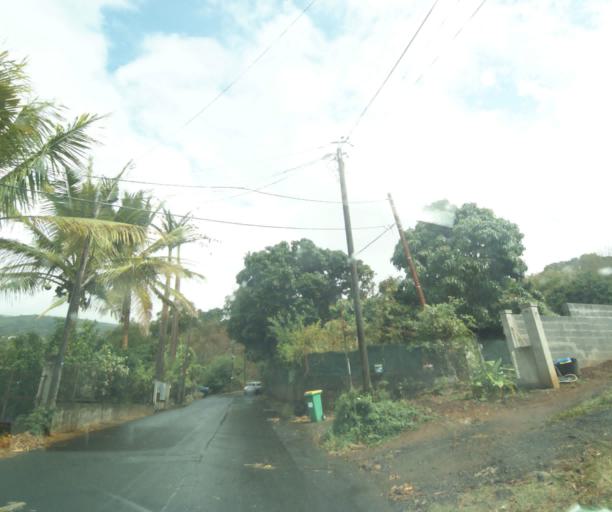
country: RE
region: Reunion
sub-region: Reunion
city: La Possession
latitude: -20.9763
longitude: 55.3302
